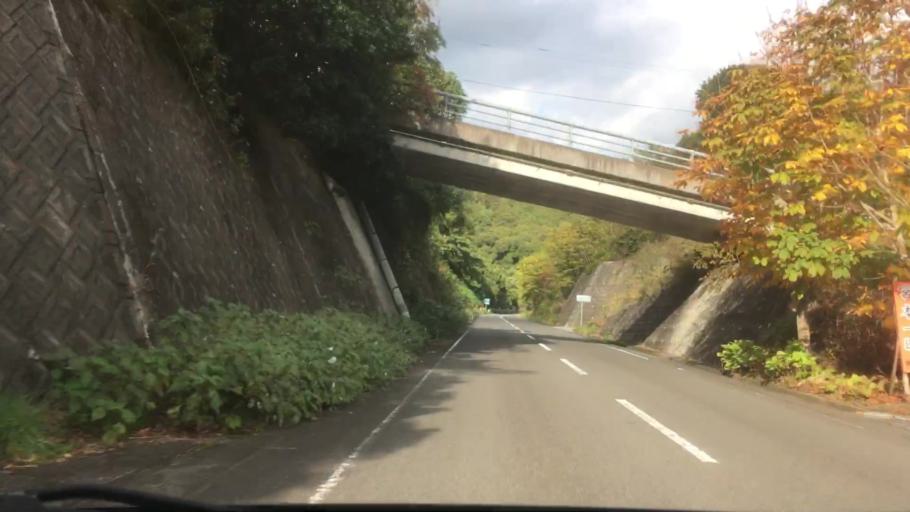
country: JP
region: Nagasaki
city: Sasebo
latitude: 32.9966
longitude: 129.7111
